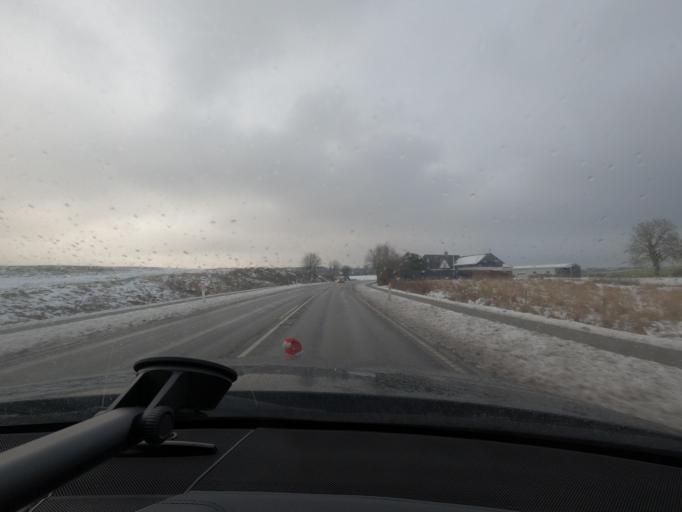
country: DK
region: South Denmark
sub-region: Sonderborg Kommune
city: Broager
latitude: 54.9028
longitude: 9.6892
